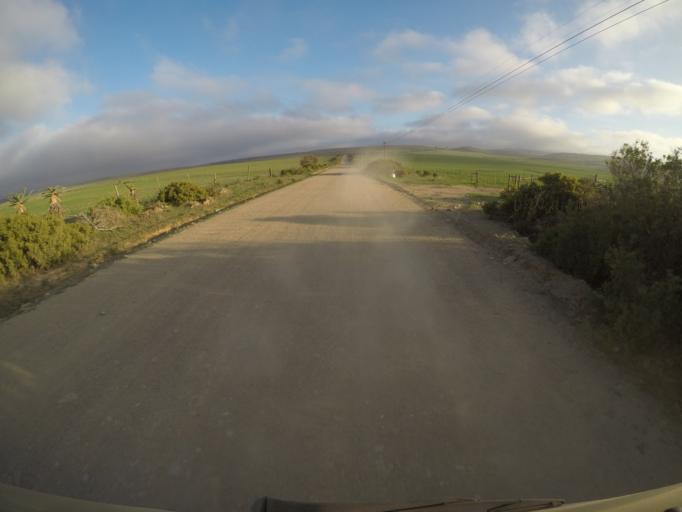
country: ZA
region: Western Cape
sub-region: Eden District Municipality
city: Mossel Bay
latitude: -34.1151
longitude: 22.0533
